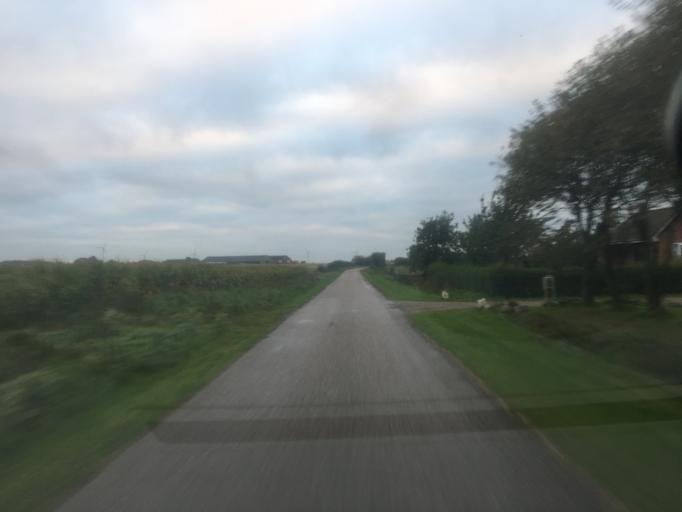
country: DK
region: South Denmark
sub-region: Tonder Kommune
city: Tonder
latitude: 54.9888
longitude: 8.9174
